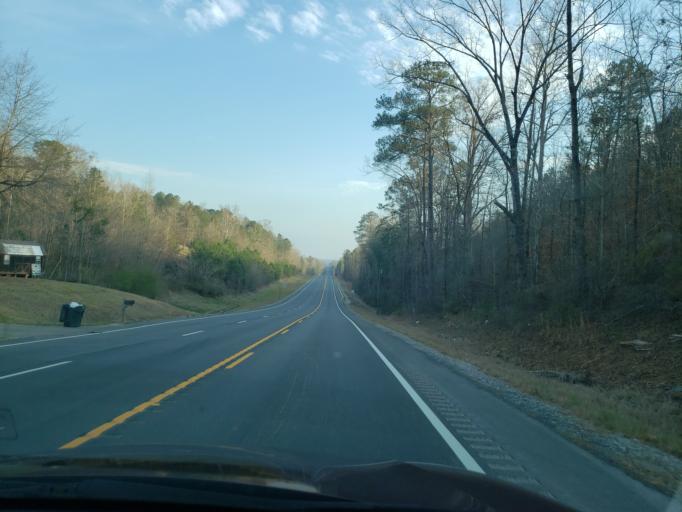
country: US
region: Alabama
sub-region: Hale County
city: Moundville
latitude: 32.8558
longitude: -87.6134
